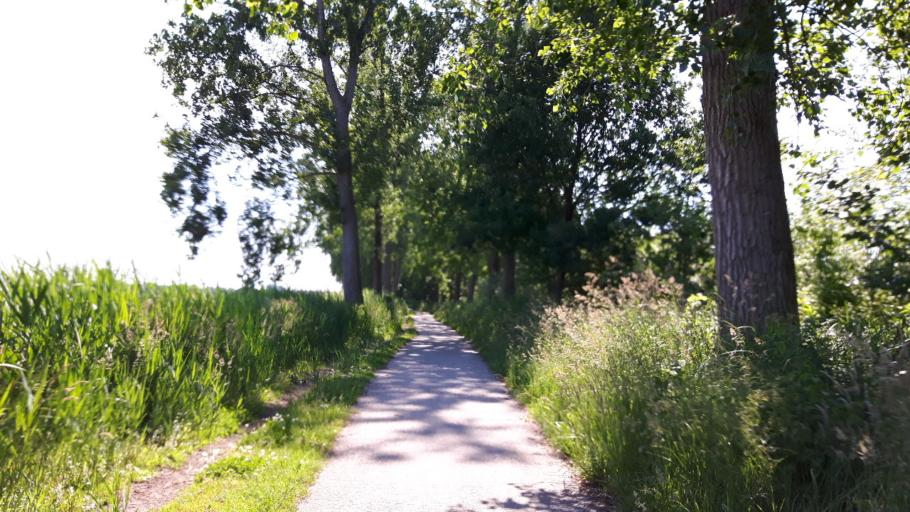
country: NL
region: Utrecht
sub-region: Stichtse Vecht
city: Vreeland
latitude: 52.2586
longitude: 5.0632
